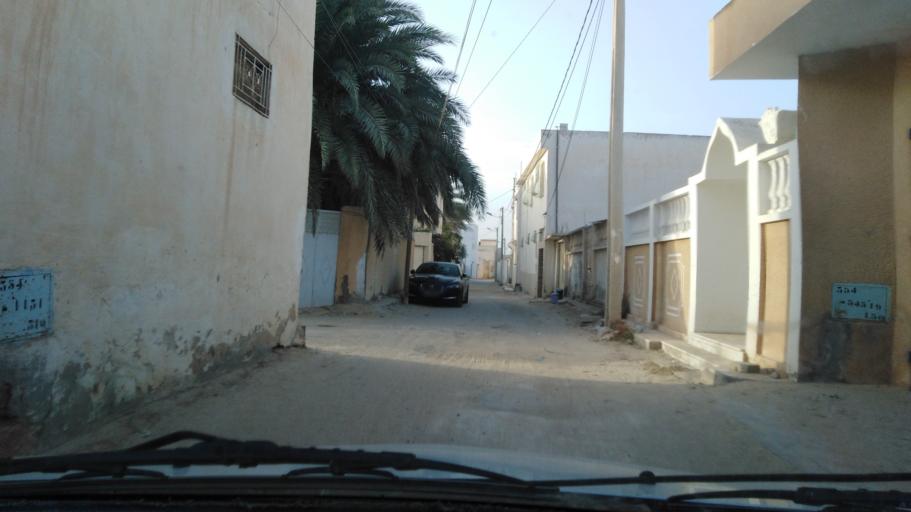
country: TN
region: Qabis
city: Gabes
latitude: 33.9571
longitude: 9.9962
